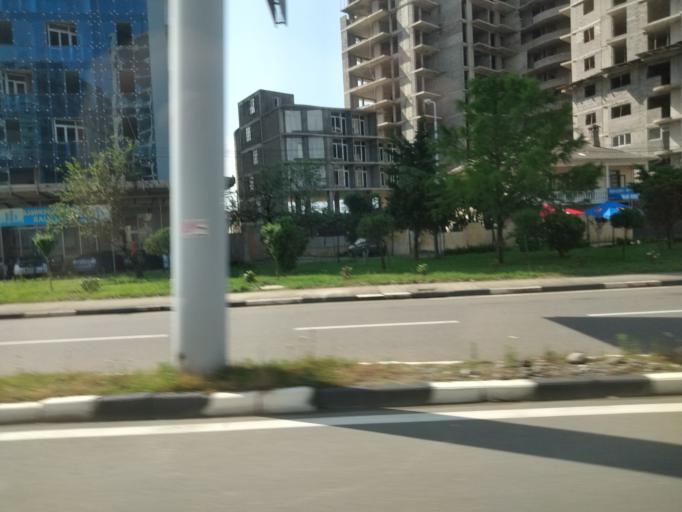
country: GE
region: Ajaria
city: Batumi
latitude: 41.6228
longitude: 41.5938
